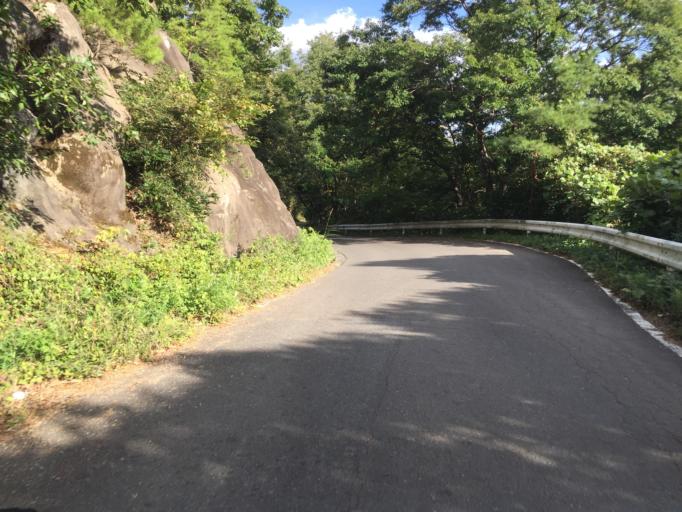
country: JP
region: Fukushima
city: Nihommatsu
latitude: 37.6755
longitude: 140.3679
